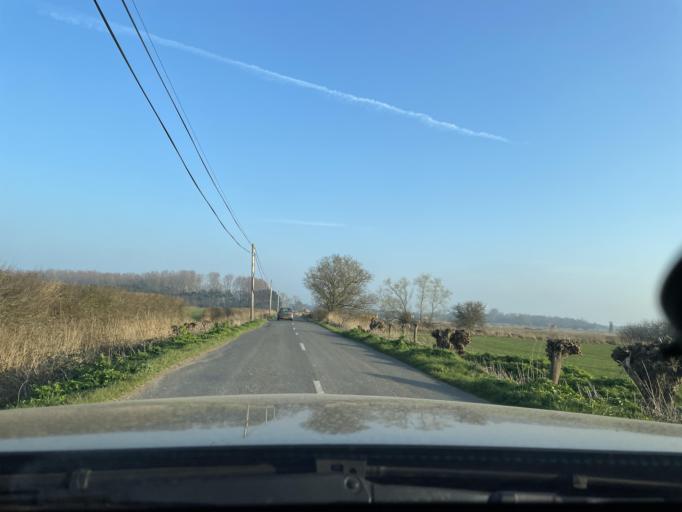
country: GB
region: England
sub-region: Norfolk
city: Martham
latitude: 52.7297
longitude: 1.6477
